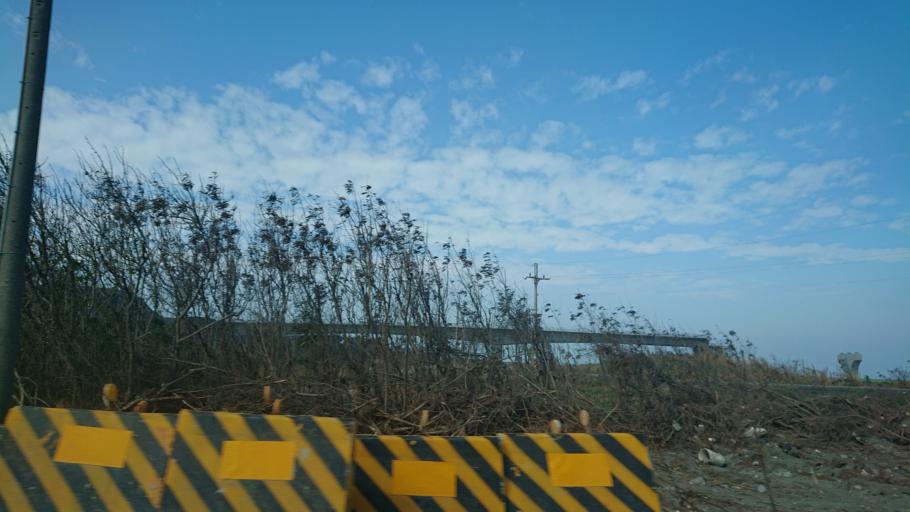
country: TW
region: Taiwan
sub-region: Changhua
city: Chang-hua
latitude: 23.9124
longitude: 120.3108
